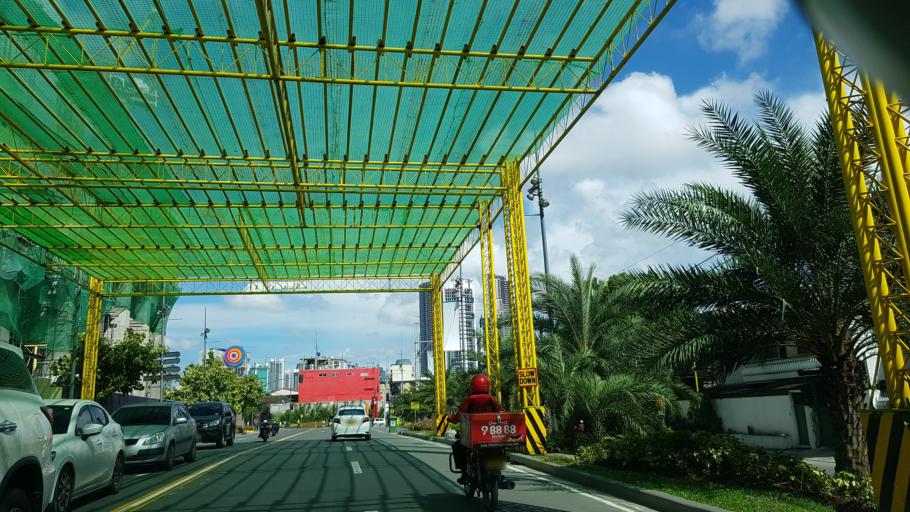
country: PH
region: Metro Manila
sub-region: Mandaluyong
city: Mandaluyong City
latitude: 14.5725
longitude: 121.0178
